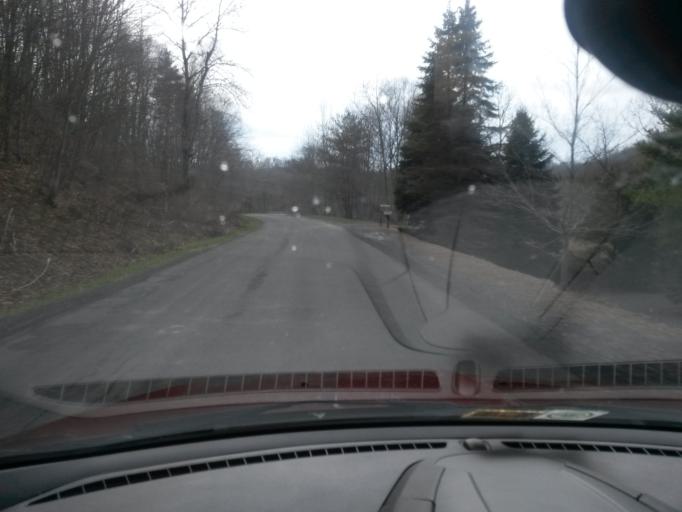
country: US
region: Virginia
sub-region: Bath County
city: Warm Springs
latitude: 38.0834
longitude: -79.8008
